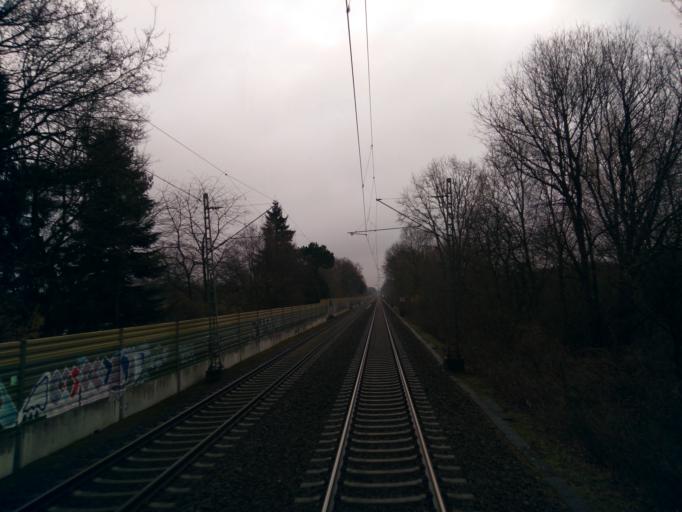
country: DE
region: Lower Saxony
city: Lilienthal
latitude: 53.0960
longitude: 8.8905
